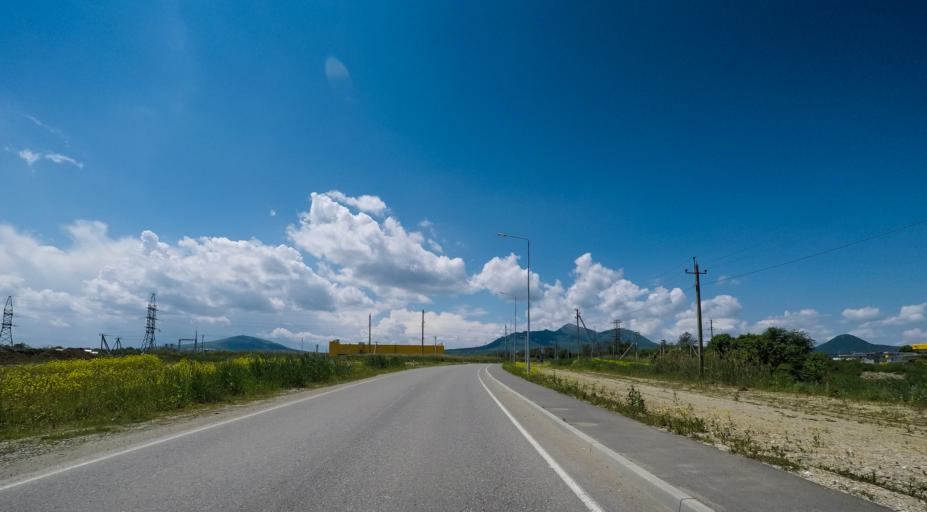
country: RU
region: Stavropol'skiy
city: Zmeyka
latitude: 44.1274
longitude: 43.1209
